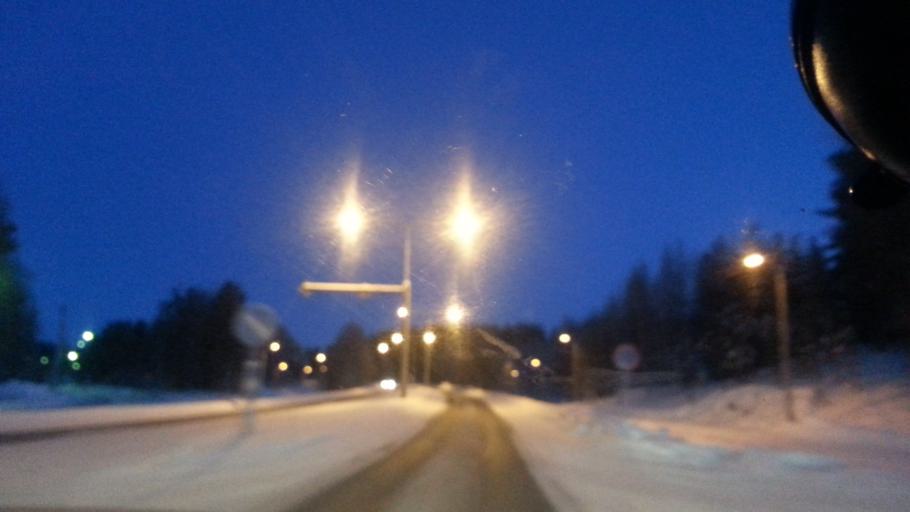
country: FI
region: Lapland
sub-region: Rovaniemi
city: Rovaniemi
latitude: 66.4905
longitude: 25.7563
